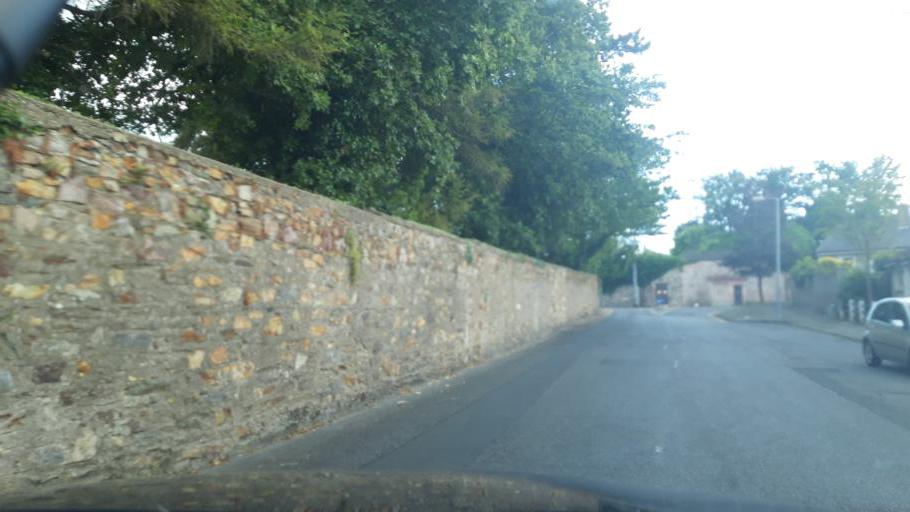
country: IE
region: Munster
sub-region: Waterford
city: Waterford
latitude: 52.2515
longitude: -7.1023
